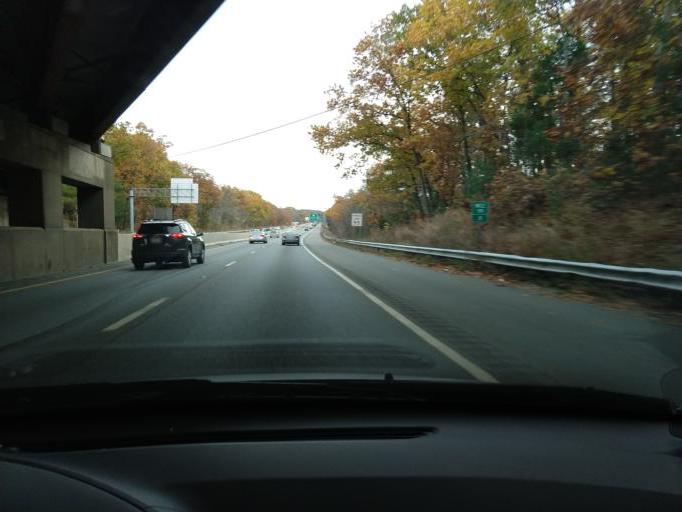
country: US
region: Massachusetts
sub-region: Worcester County
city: Leominster
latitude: 42.5430
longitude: -71.7524
